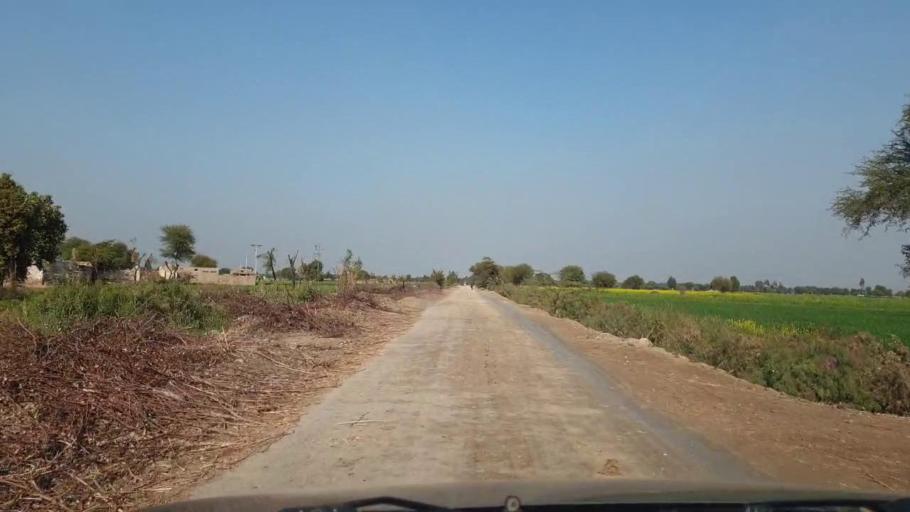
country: PK
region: Sindh
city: Jhol
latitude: 25.9345
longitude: 68.8785
